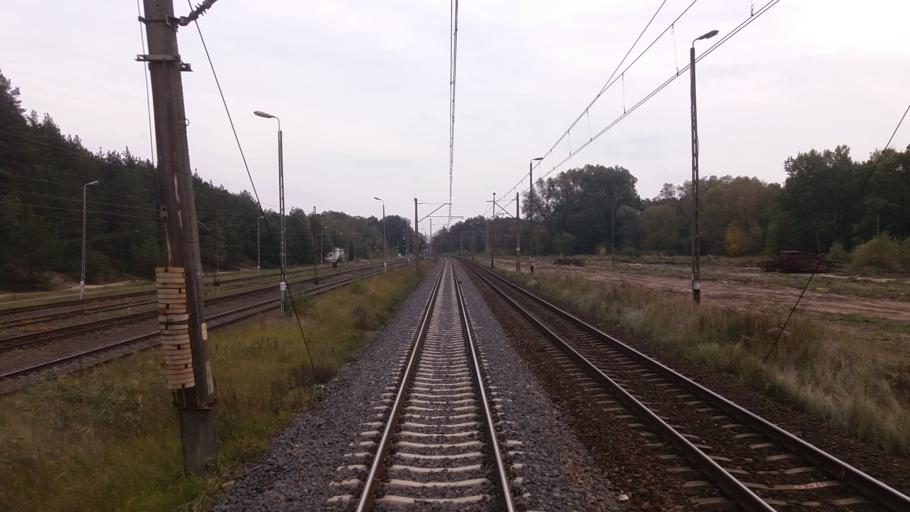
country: PL
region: West Pomeranian Voivodeship
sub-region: Powiat gryfinski
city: Stare Czarnowo
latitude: 53.3896
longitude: 14.7057
